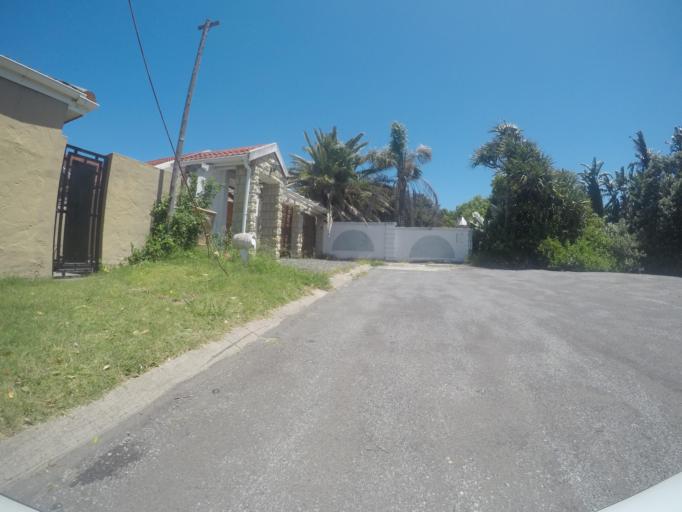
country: ZA
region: Eastern Cape
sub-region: Buffalo City Metropolitan Municipality
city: East London
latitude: -32.9563
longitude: 27.9997
